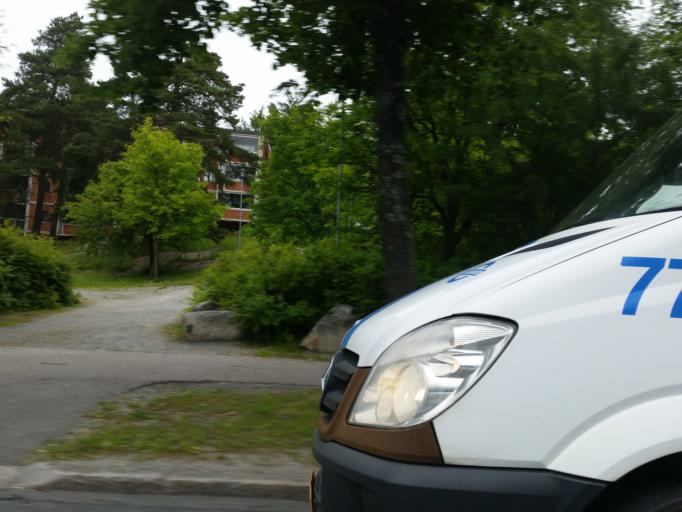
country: FI
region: Northern Savo
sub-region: Kuopio
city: Kuopio
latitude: 62.8822
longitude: 27.6694
